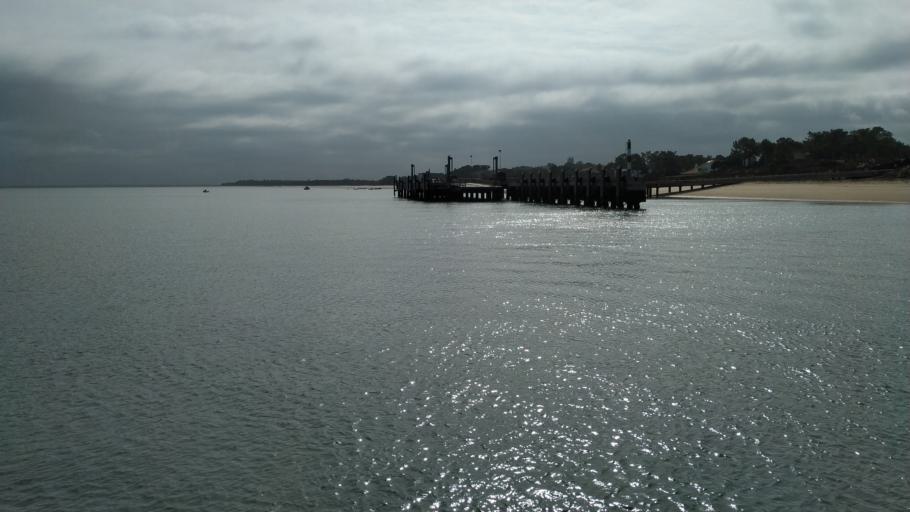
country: PT
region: Setubal
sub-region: Setubal
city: Setubal
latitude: 38.4687
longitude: -8.8641
